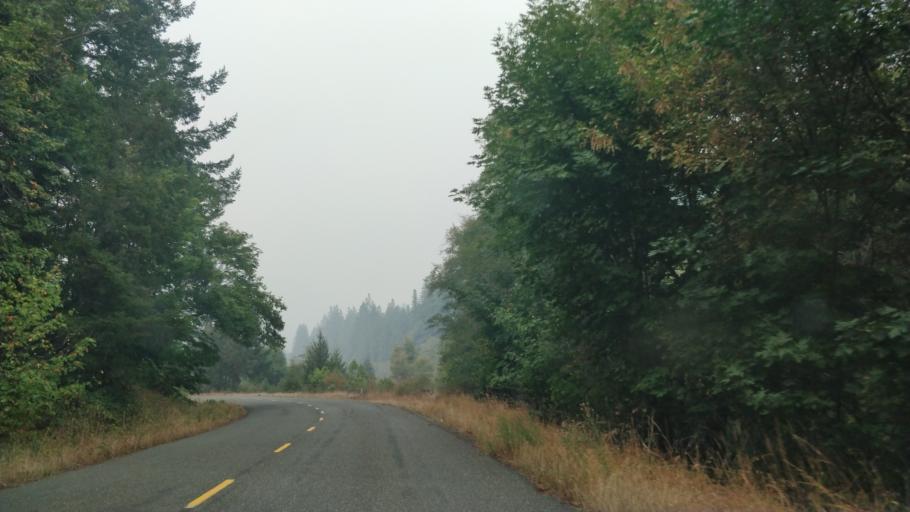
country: US
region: California
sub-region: Humboldt County
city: Rio Dell
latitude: 40.3397
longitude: -124.0269
